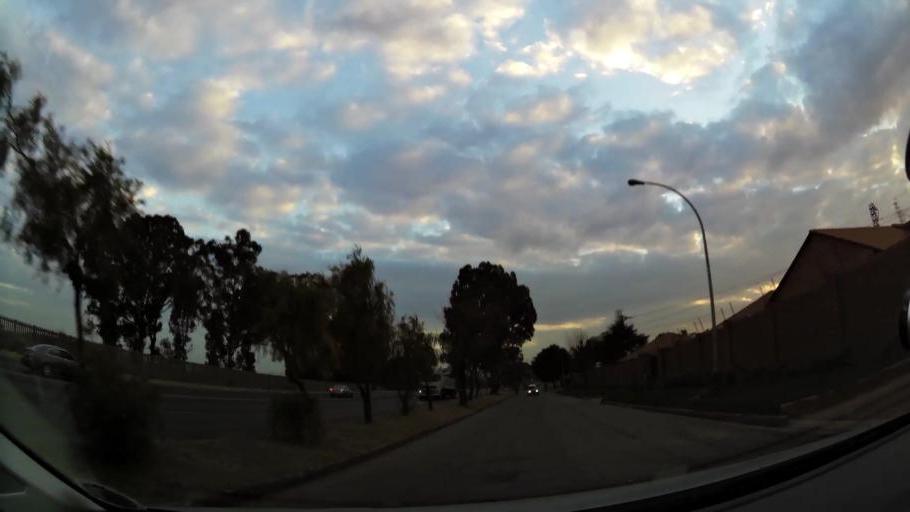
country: ZA
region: Gauteng
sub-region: Ekurhuleni Metropolitan Municipality
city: Germiston
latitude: -26.2026
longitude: 28.1395
